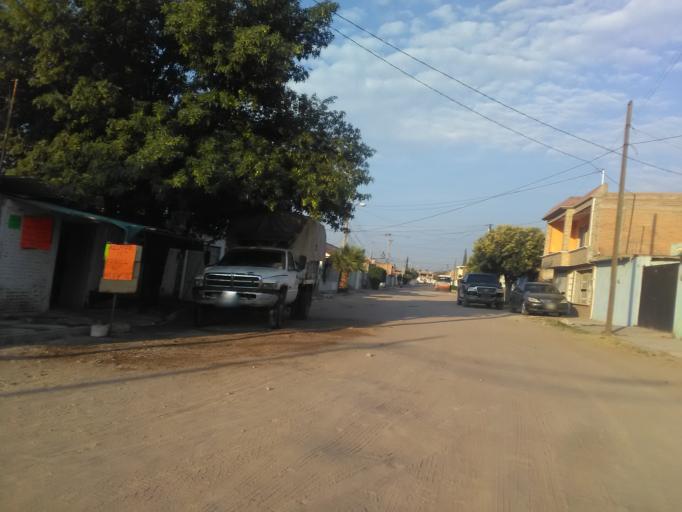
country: MX
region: Durango
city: Victoria de Durango
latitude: 24.0504
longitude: -104.6457
